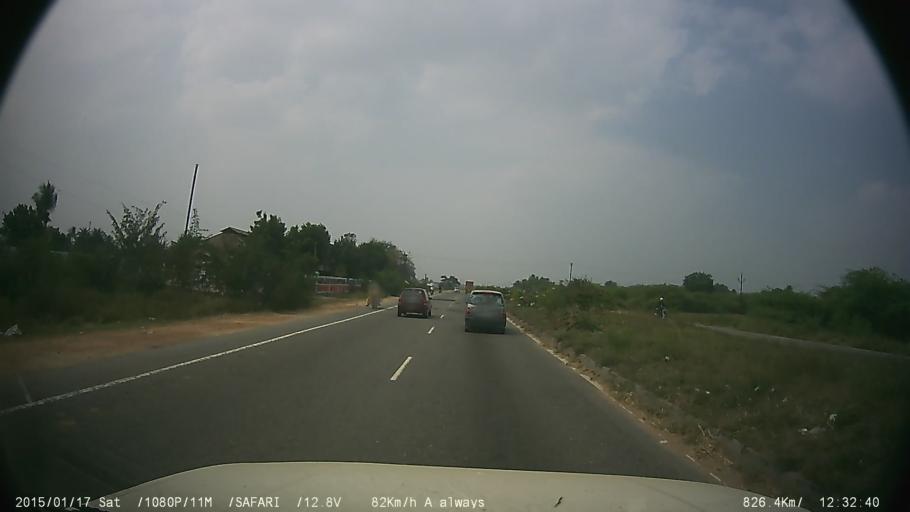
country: IN
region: Tamil Nadu
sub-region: Kancheepuram
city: Kanchipuram
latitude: 12.8701
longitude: 79.6442
